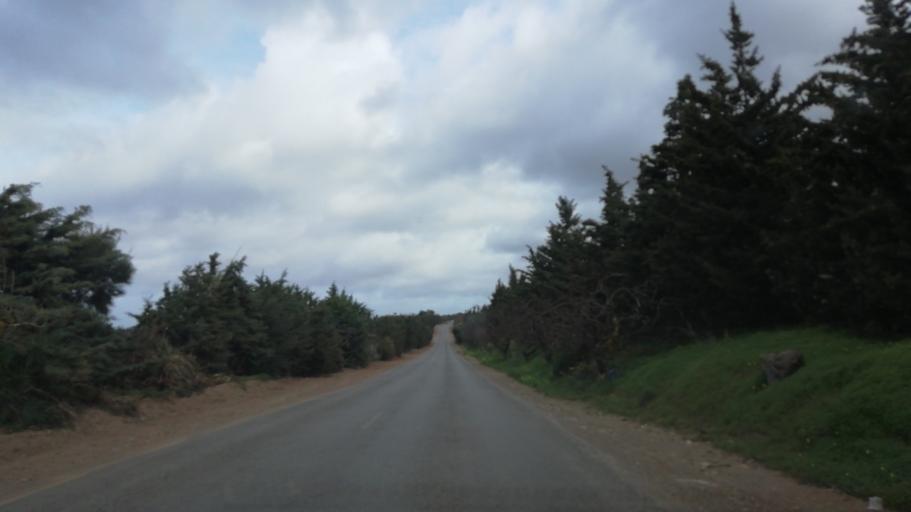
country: DZ
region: Oran
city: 'Ain el Turk
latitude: 35.7010
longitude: -0.8457
